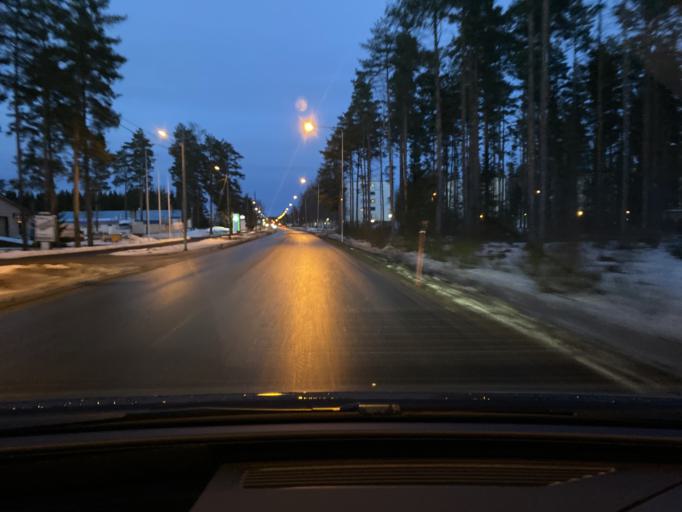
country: FI
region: Varsinais-Suomi
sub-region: Loimaa
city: Loimaa
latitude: 60.8487
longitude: 23.0358
